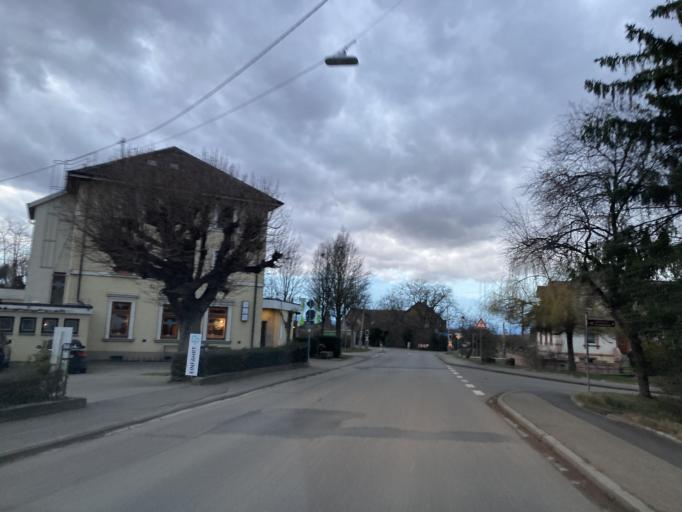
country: DE
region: Baden-Wuerttemberg
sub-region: Freiburg Region
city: Vogtsburg
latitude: 48.0905
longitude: 7.6224
